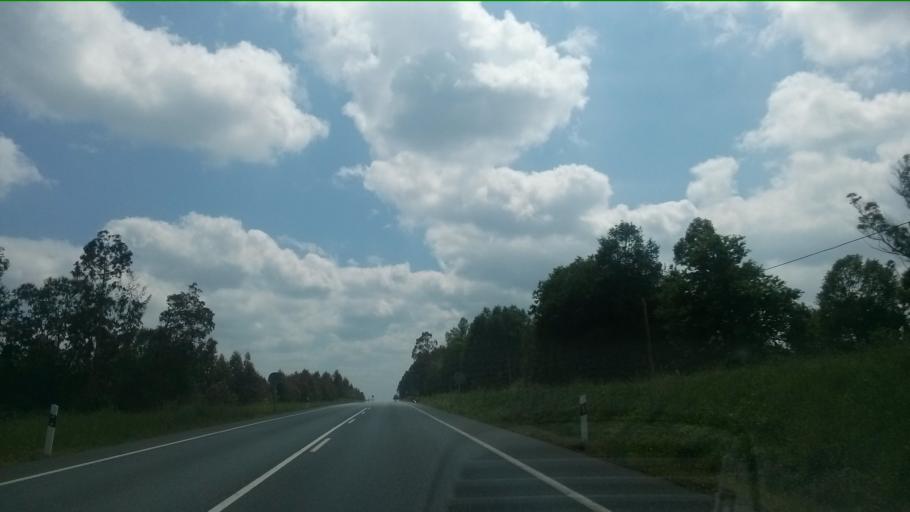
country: ES
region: Galicia
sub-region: Provincia da Coruna
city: Mesia
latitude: 43.0834
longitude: -8.1914
